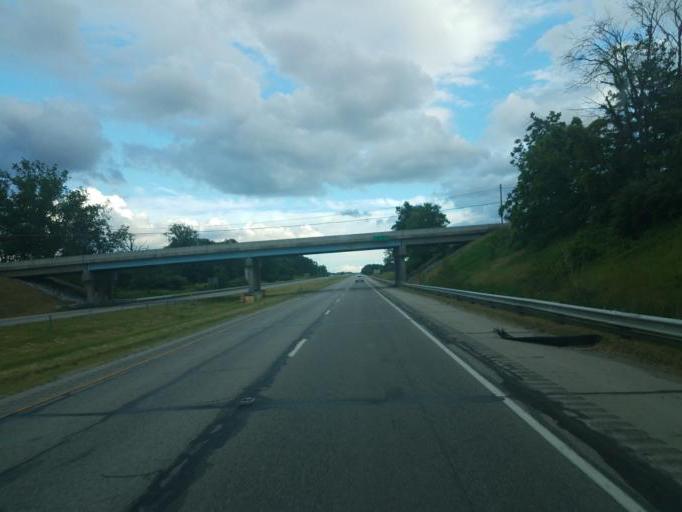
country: US
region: Indiana
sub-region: DeKalb County
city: Garrett
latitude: 41.3090
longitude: -85.0878
